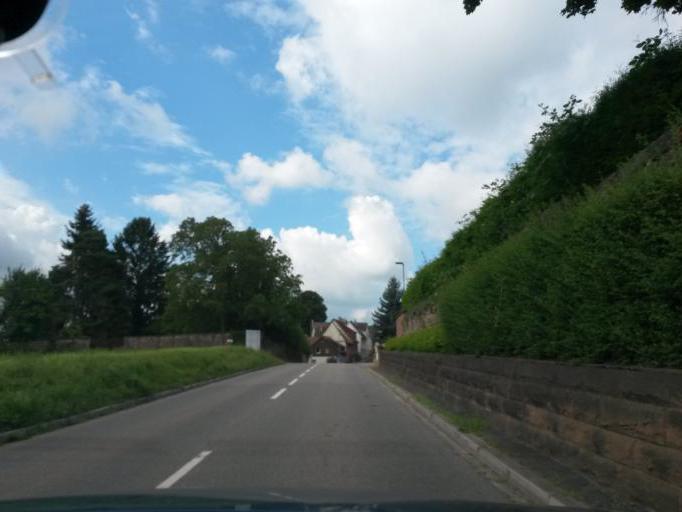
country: DE
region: Baden-Wuerttemberg
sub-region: Karlsruhe Region
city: Neuenburg
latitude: 48.8897
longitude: 8.5463
